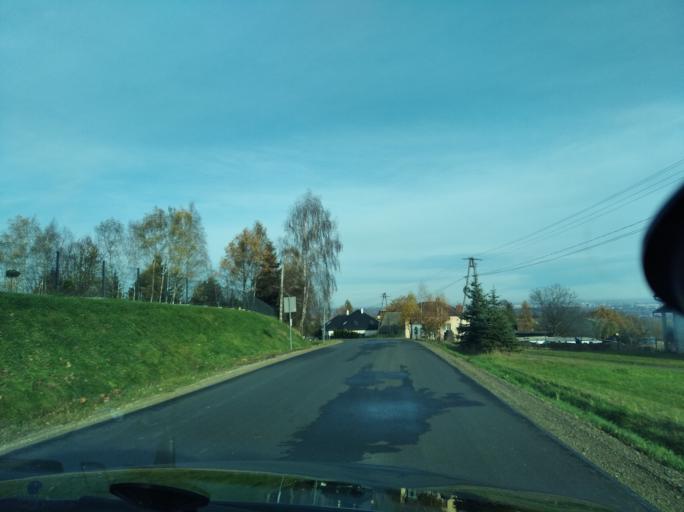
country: PL
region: Subcarpathian Voivodeship
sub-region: Powiat rzeszowski
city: Straszydle
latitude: 49.9354
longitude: 21.9812
